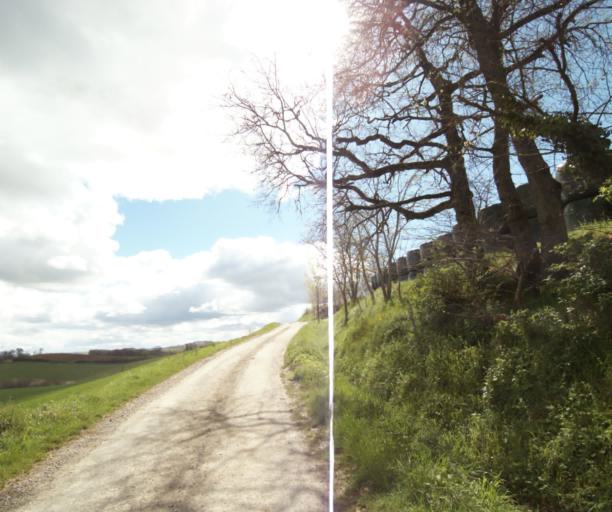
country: FR
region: Midi-Pyrenees
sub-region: Departement de l'Ariege
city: Saverdun
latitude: 43.1955
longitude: 1.5402
